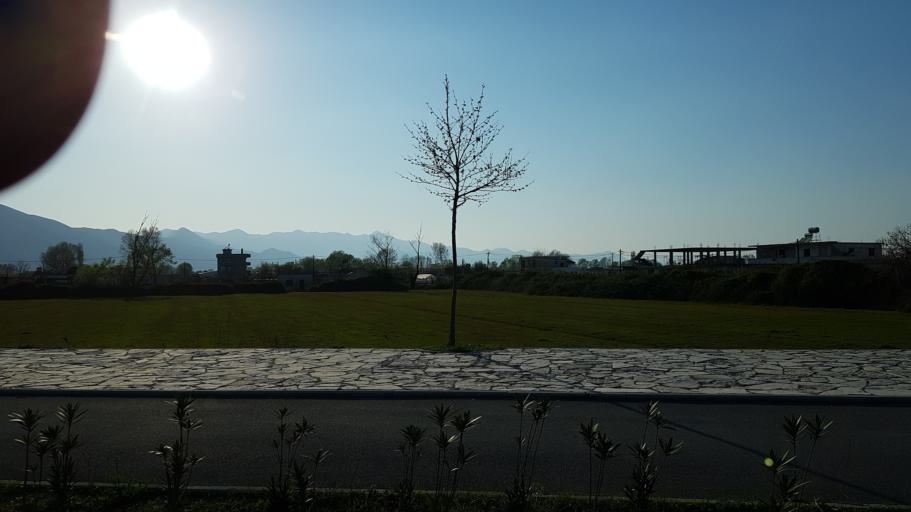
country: AL
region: Shkoder
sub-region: Rrethi i Shkodres
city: Shkoder
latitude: 42.0774
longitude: 19.4916
